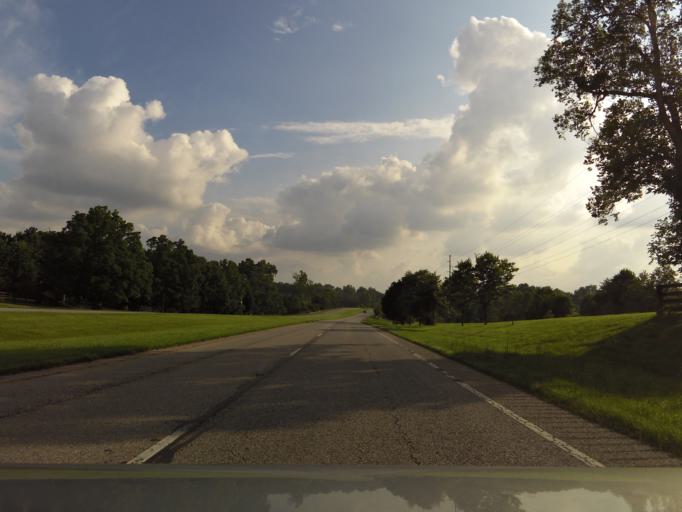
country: US
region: Kentucky
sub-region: Bourbon County
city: Paris
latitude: 38.1601
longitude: -84.3280
